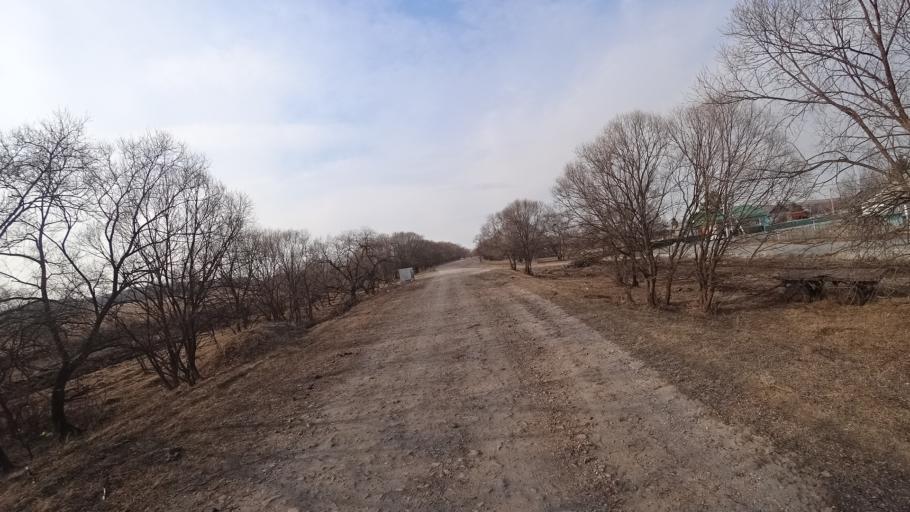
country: RU
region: Amur
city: Novobureyskiy
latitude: 49.8960
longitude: 129.8745
